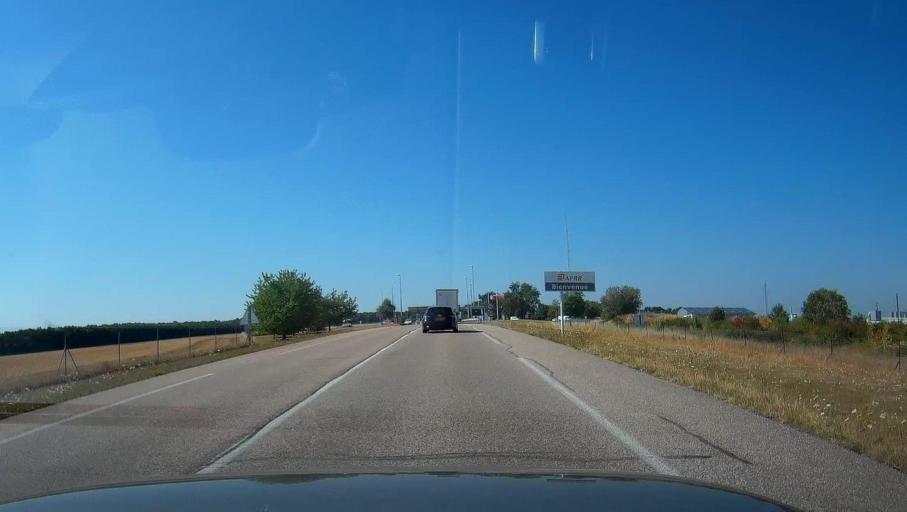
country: FR
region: Lorraine
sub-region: Departement de Meurthe-et-Moselle
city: Colombey-les-Belles
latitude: 48.5429
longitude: 5.9100
